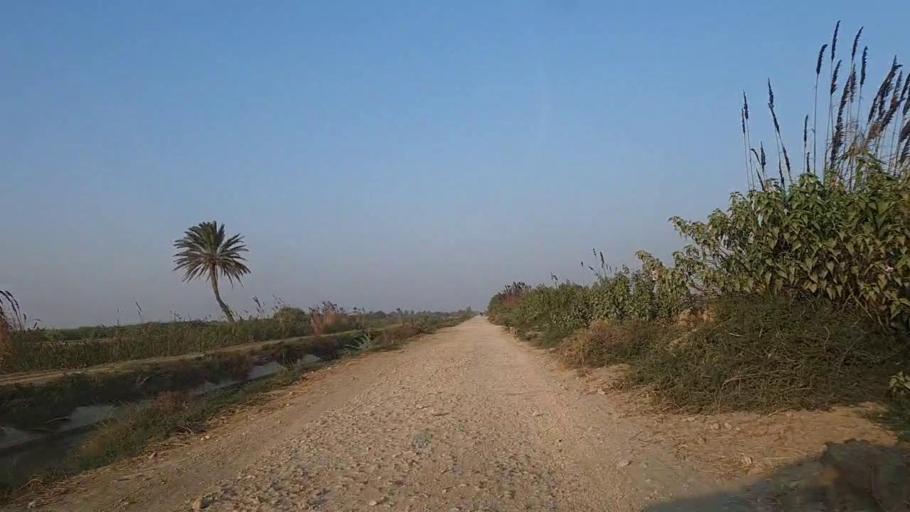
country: PK
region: Sindh
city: Keti Bandar
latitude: 24.2788
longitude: 67.6858
